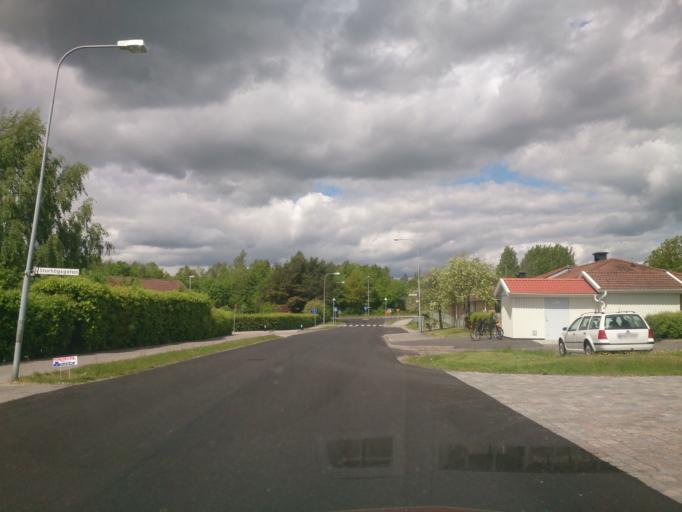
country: SE
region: OEstergoetland
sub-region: Norrkopings Kommun
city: Norrkoping
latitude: 58.5661
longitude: 16.2251
